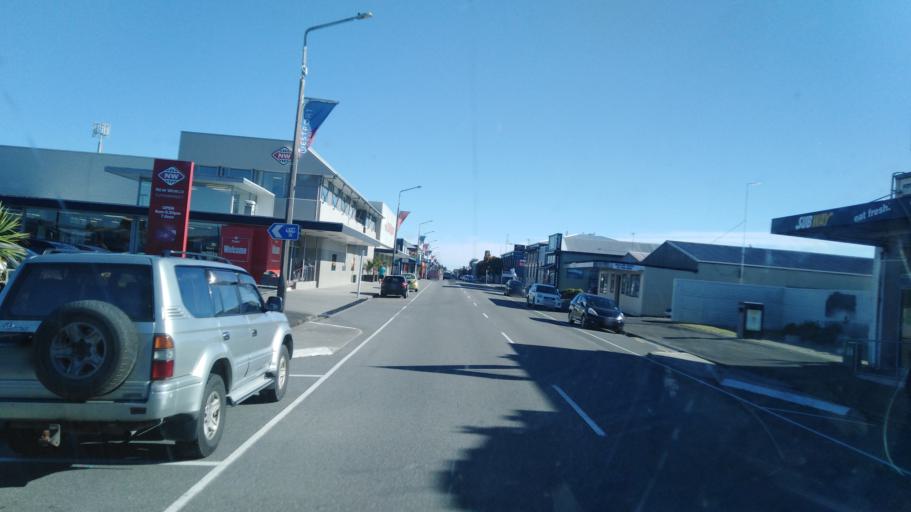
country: NZ
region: West Coast
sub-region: Buller District
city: Westport
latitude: -41.7579
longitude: 171.5993
